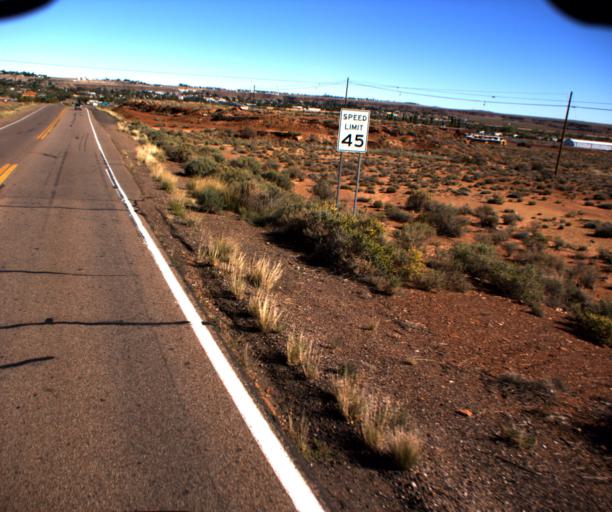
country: US
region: Arizona
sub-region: Navajo County
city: Holbrook
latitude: 34.8865
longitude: -110.1626
